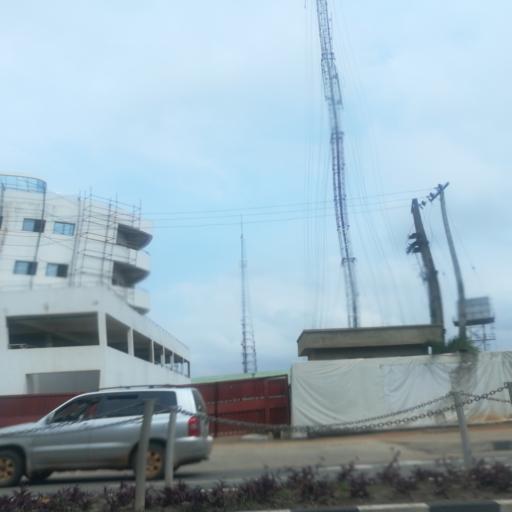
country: NG
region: Lagos
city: Ikeja
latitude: 6.6164
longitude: 3.3641
